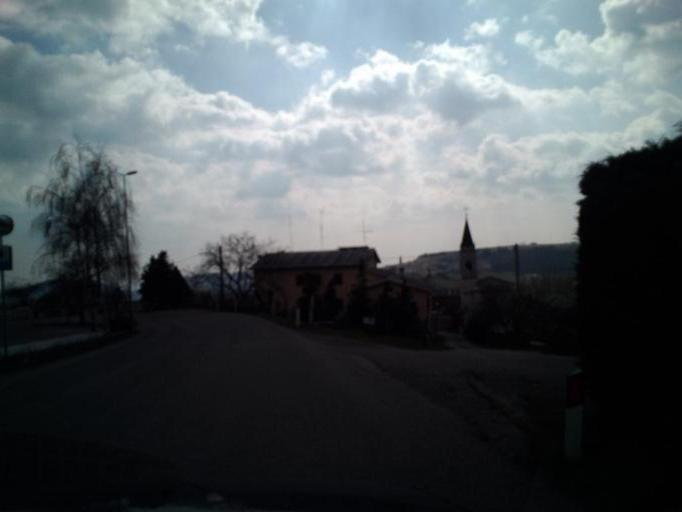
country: IT
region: Veneto
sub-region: Provincia di Verona
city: Sant'Anna d'Alfaedo
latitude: 45.6401
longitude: 10.9639
